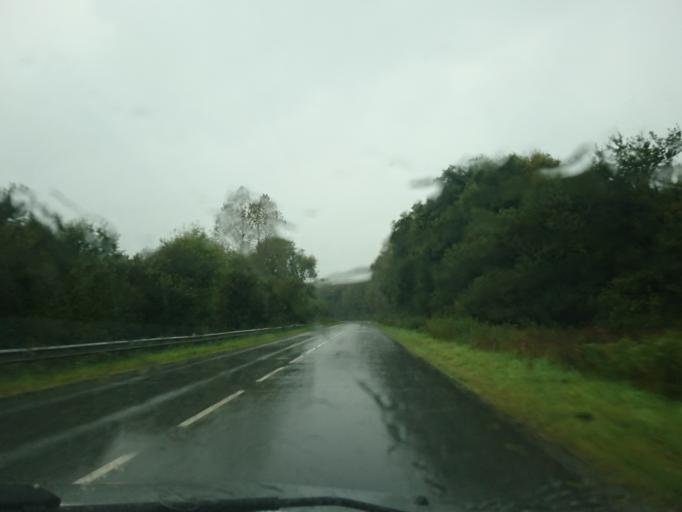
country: FR
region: Brittany
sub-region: Departement du Finistere
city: Plouvien
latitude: 48.5382
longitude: -4.4825
